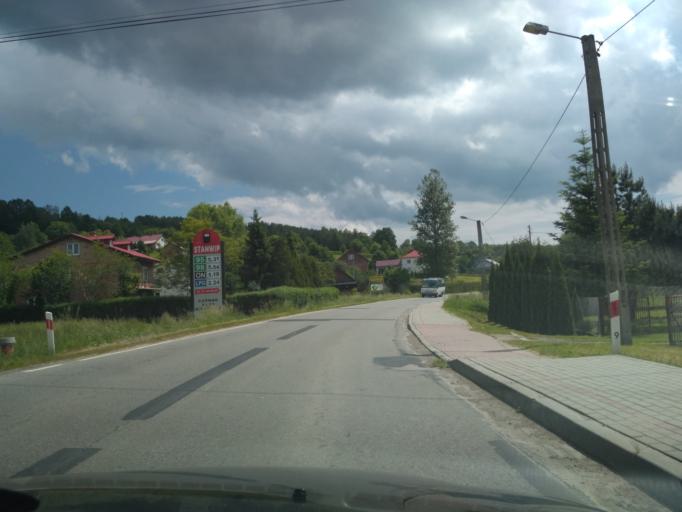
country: PL
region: Subcarpathian Voivodeship
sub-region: Powiat rzeszowski
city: Hyzne
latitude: 49.9286
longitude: 22.1554
